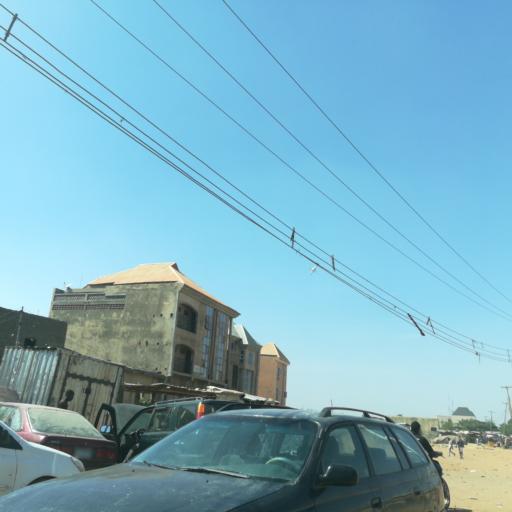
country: NG
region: Kano
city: Kano
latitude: 11.9954
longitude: 8.5311
